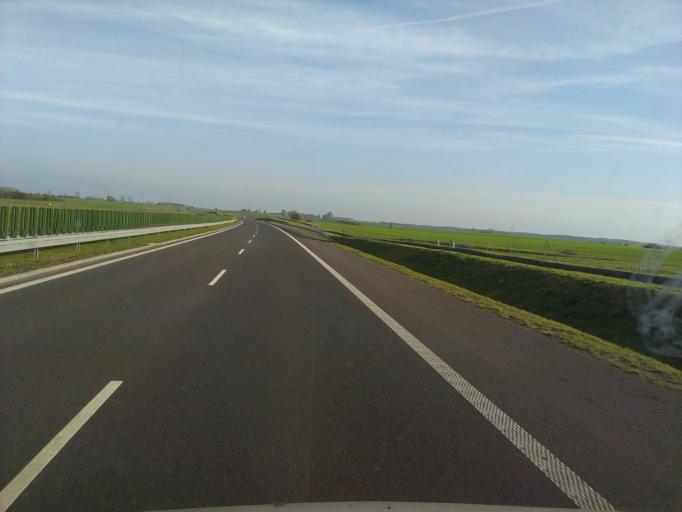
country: PL
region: West Pomeranian Voivodeship
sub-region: Powiat pyrzycki
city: Kozielice
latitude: 53.1029
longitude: 14.7738
